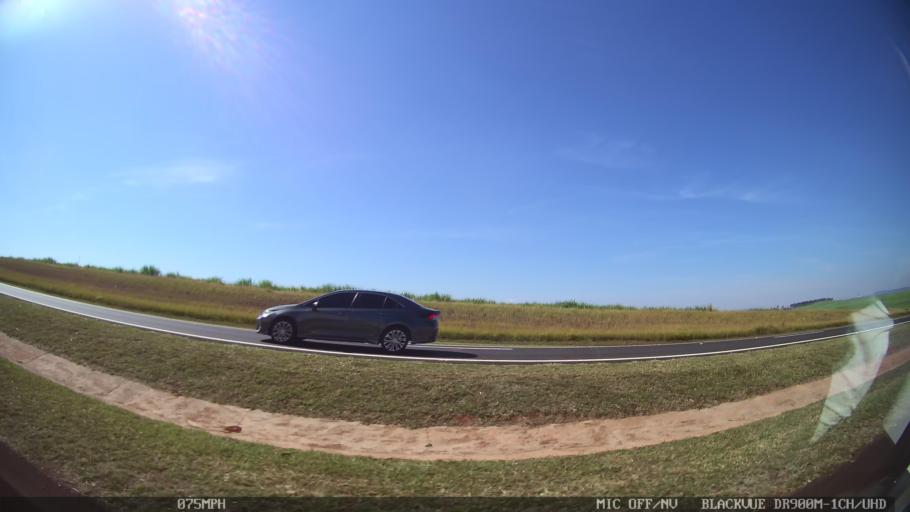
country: BR
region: Sao Paulo
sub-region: Ribeirao Preto
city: Ribeirao Preto
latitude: -21.1747
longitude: -47.8960
